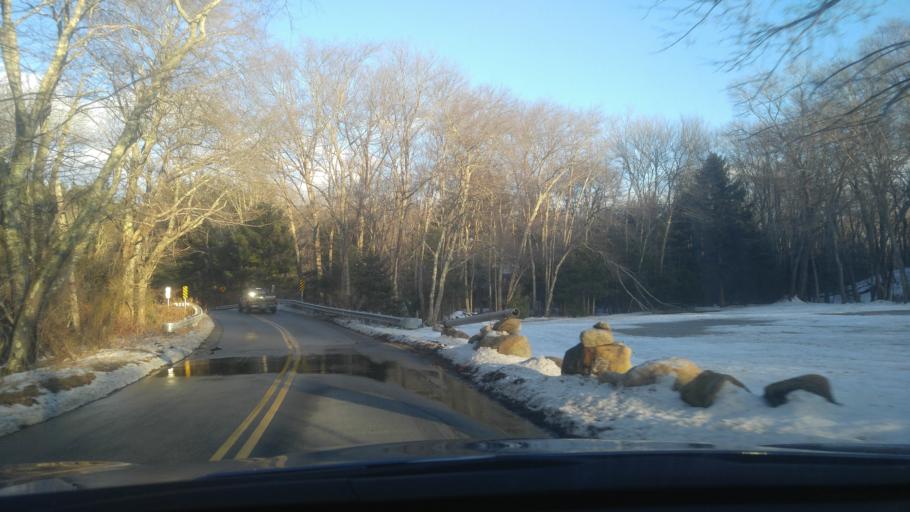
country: US
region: Rhode Island
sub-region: Kent County
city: Coventry
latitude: 41.7190
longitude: -71.6655
